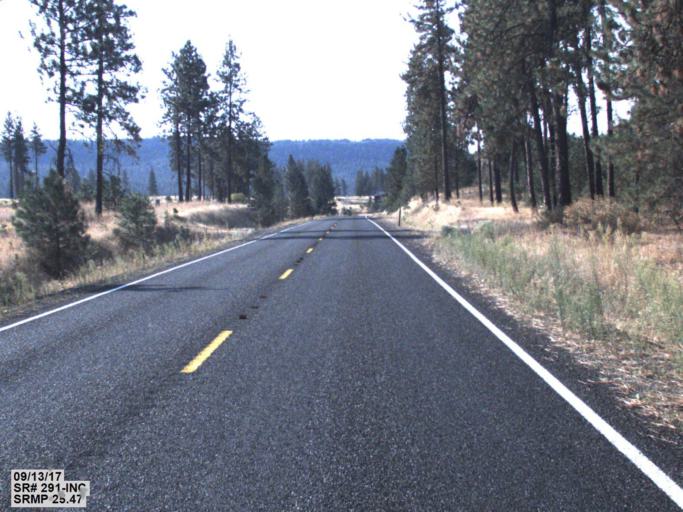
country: US
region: Washington
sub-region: Spokane County
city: Airway Heights
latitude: 47.8592
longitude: -117.7121
